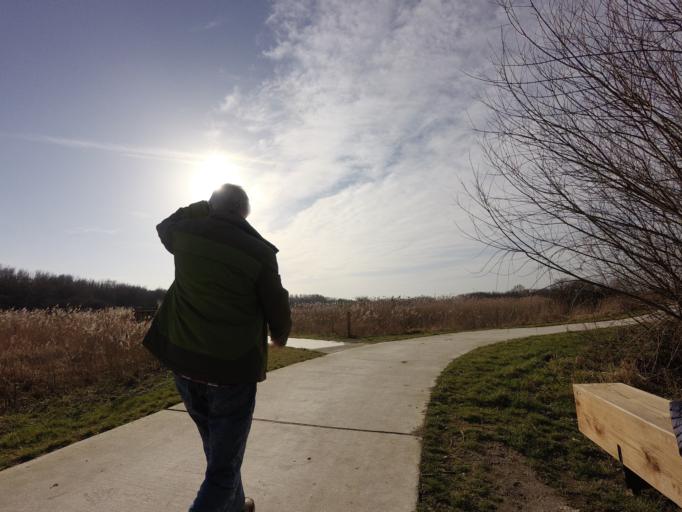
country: NL
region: Flevoland
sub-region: Gemeente Almere
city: Almere Stad
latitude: 52.3396
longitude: 5.1818
